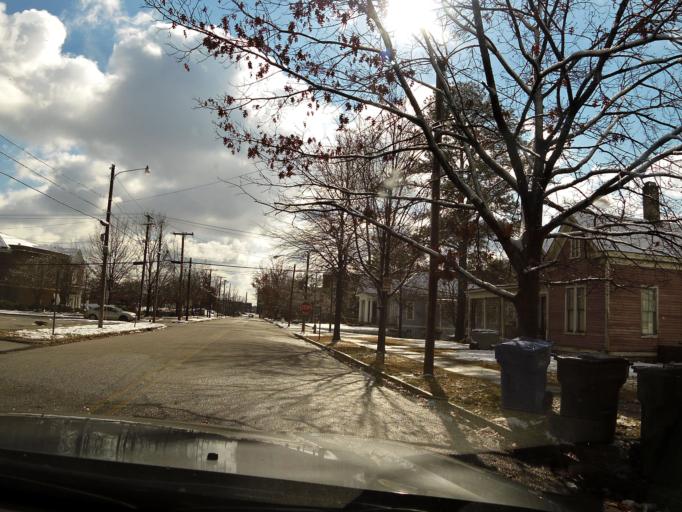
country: US
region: North Carolina
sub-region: Wilson County
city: Wilson
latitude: 35.7281
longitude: -77.9155
